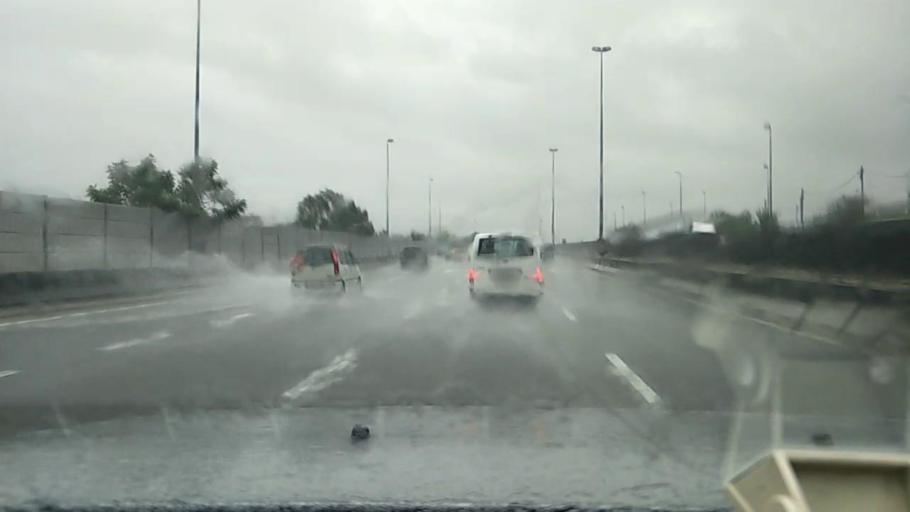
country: MY
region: Selangor
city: Kampong Baharu Balakong
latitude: 2.9904
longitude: 101.7694
